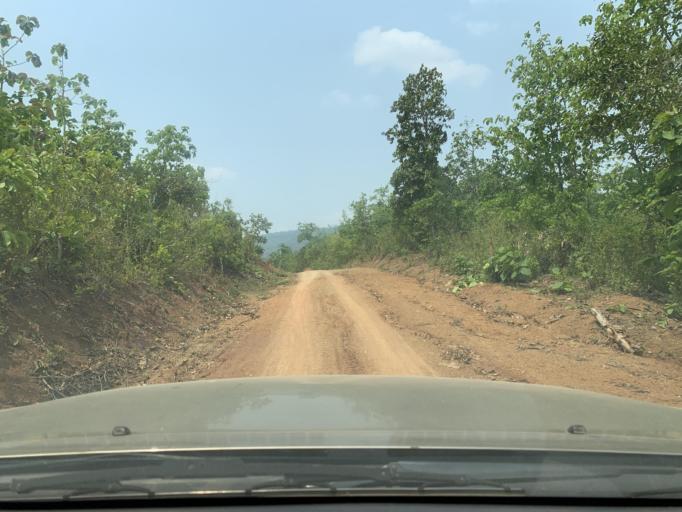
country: LA
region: Louangphabang
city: Louangphabang
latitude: 19.9378
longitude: 102.1346
